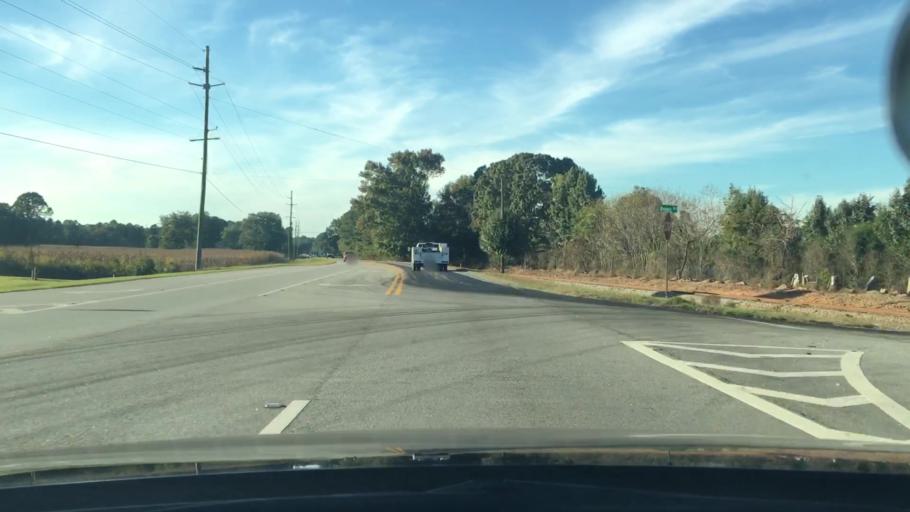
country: US
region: Georgia
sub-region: Coweta County
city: Senoia
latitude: 33.3053
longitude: -84.5981
